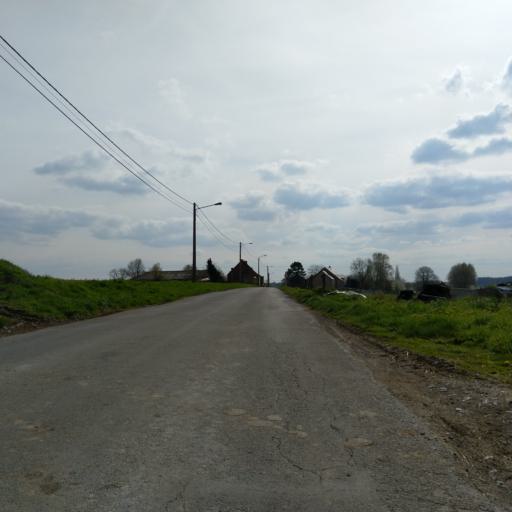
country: BE
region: Wallonia
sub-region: Province du Hainaut
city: Jurbise
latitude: 50.5290
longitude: 3.9665
